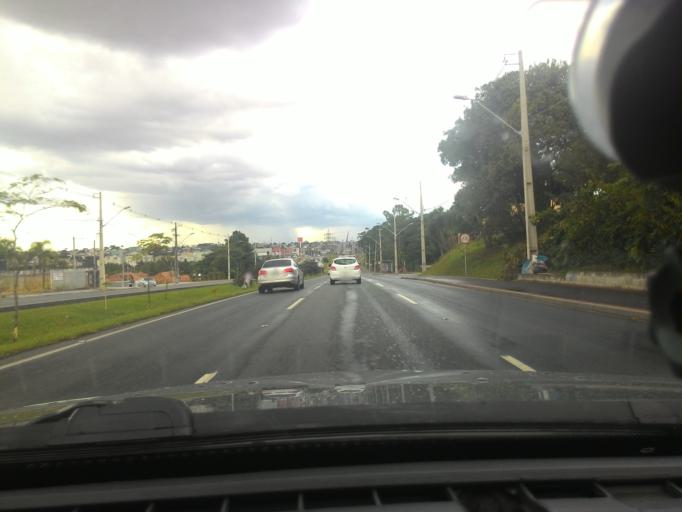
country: BR
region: Parana
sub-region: Sao Jose Dos Pinhais
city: Sao Jose dos Pinhais
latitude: -25.4884
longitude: -49.2173
